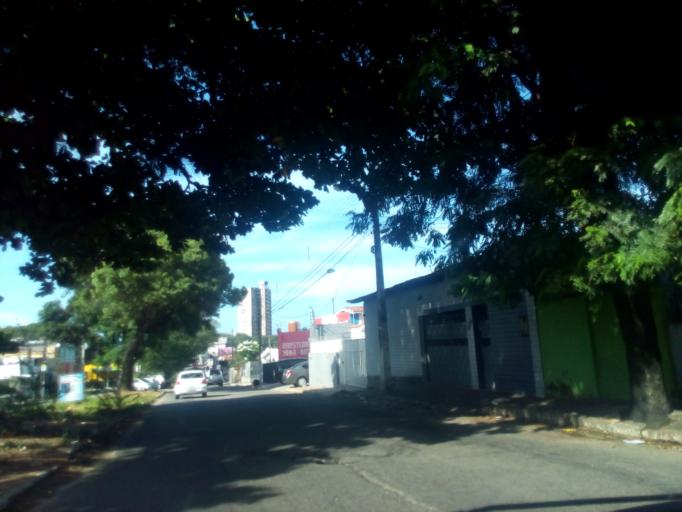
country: BR
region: Rio Grande do Norte
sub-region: Natal
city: Natal
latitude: -5.8180
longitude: -35.2147
